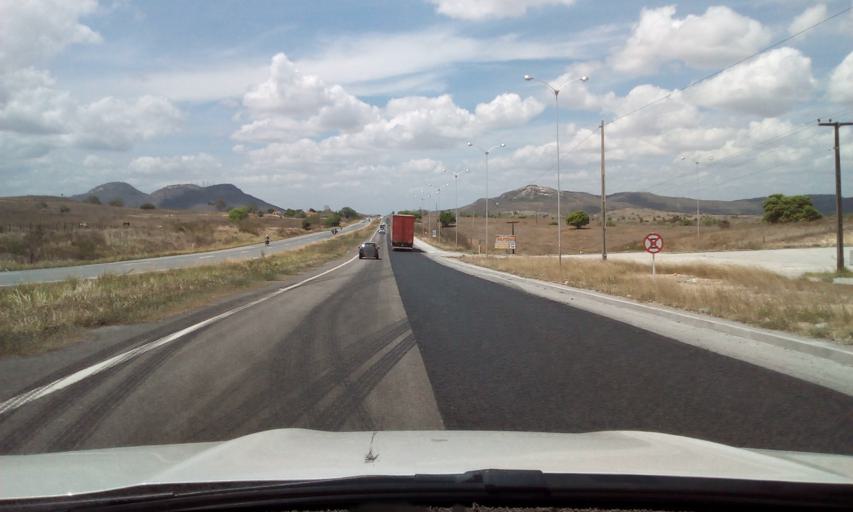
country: BR
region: Paraiba
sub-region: Gurinhem
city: Gurinhem
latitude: -7.1669
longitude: -35.3631
